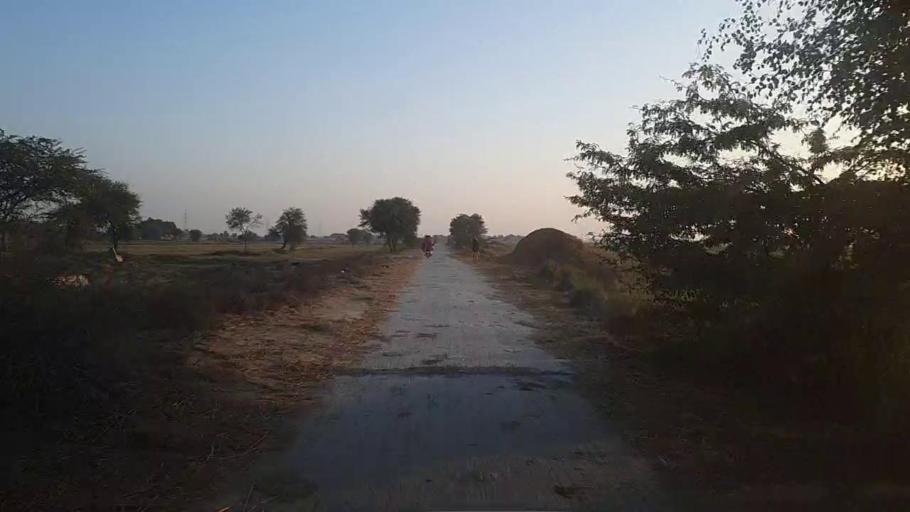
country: PK
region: Sindh
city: Khairpur Nathan Shah
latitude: 27.1798
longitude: 67.7338
